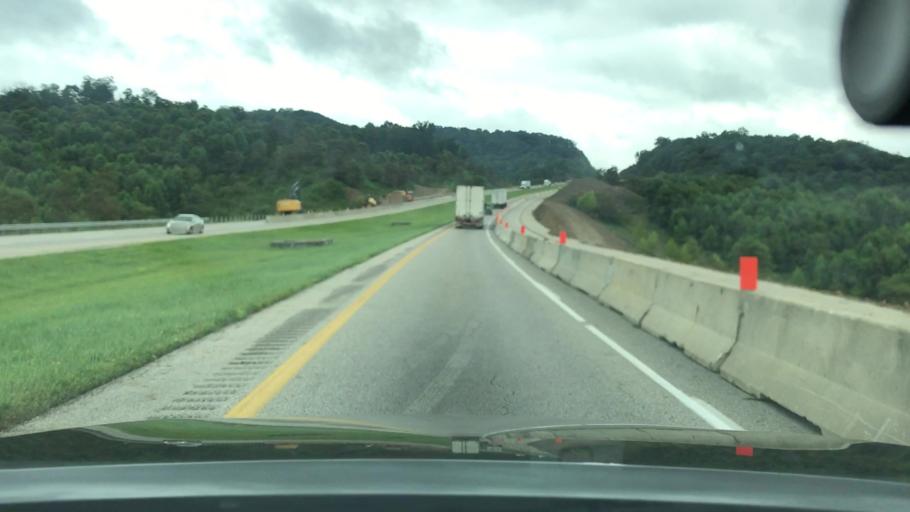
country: US
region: Ohio
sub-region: Ross County
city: Chillicothe
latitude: 39.2418
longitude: -82.8418
